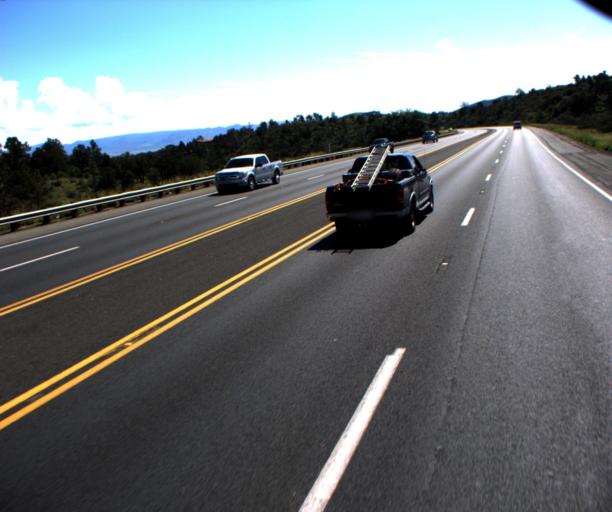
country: US
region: Arizona
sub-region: Yavapai County
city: Prescott
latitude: 34.5490
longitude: -112.3938
